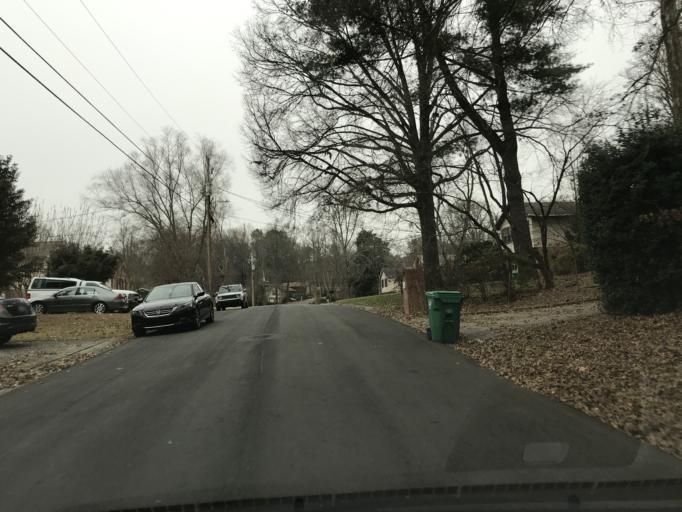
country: US
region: Georgia
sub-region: DeKalb County
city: Clarkston
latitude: 33.8174
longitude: -84.2540
